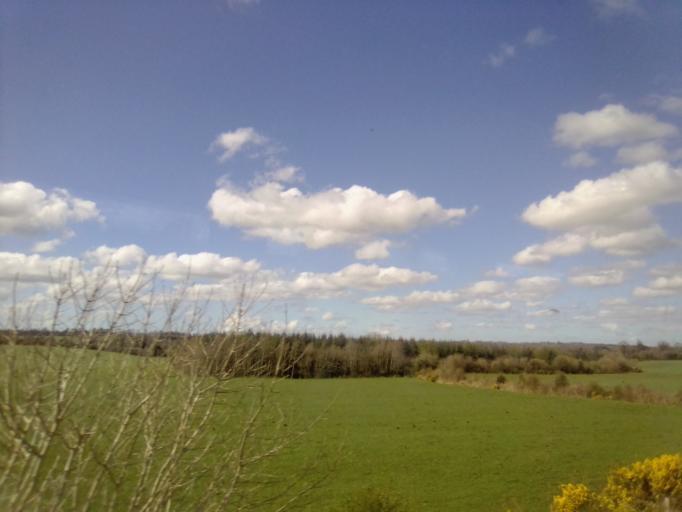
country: IE
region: Munster
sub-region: County Cork
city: Kanturk
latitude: 52.1117
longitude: -8.9373
